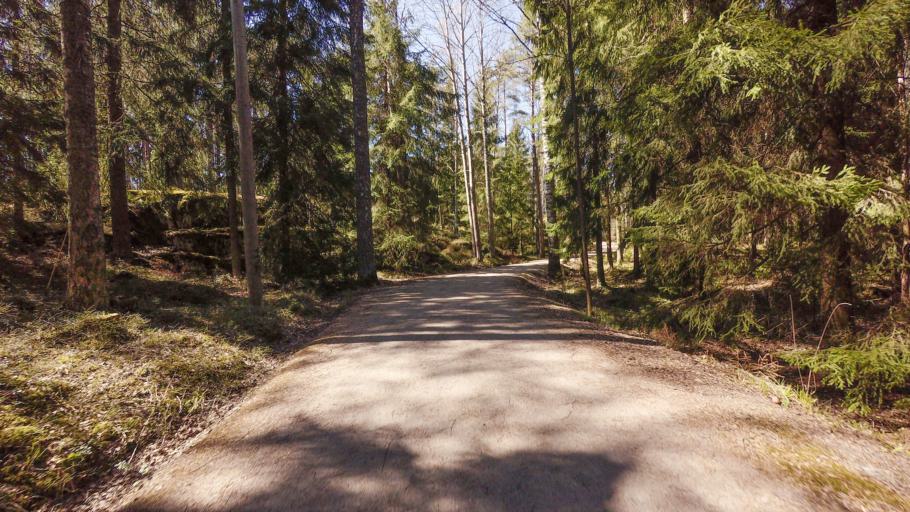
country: FI
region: Uusimaa
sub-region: Helsinki
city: Vantaa
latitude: 60.2254
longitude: 25.1428
